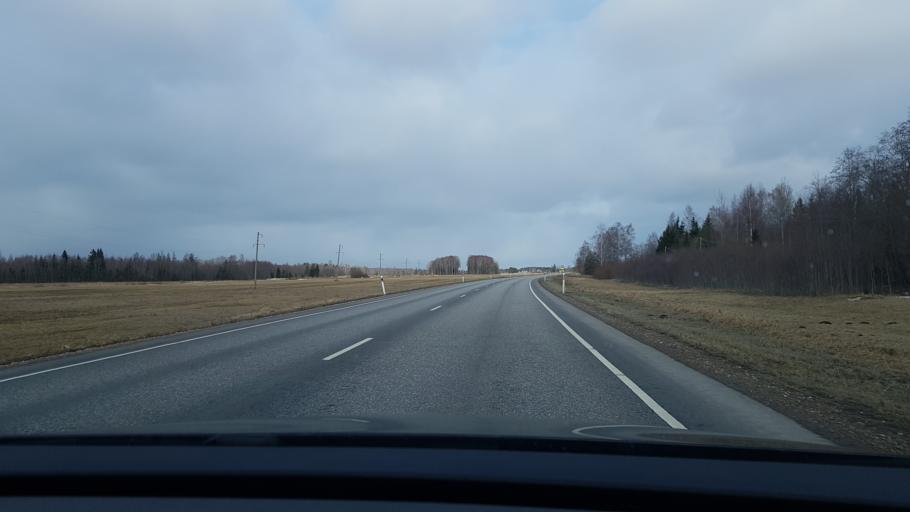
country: EE
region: Paernumaa
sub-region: Tootsi vald
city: Tootsi
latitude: 58.5919
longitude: 24.9006
